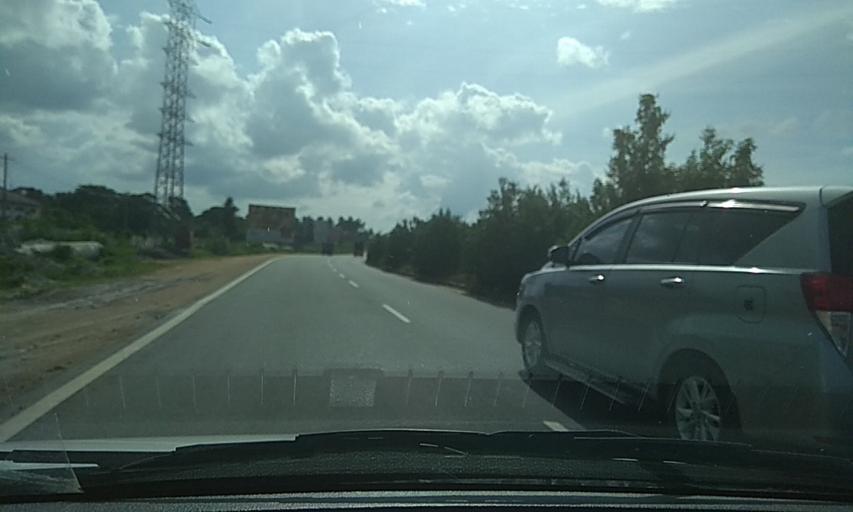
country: IN
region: Karnataka
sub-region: Mandya
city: Mandya
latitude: 12.4956
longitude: 76.8002
